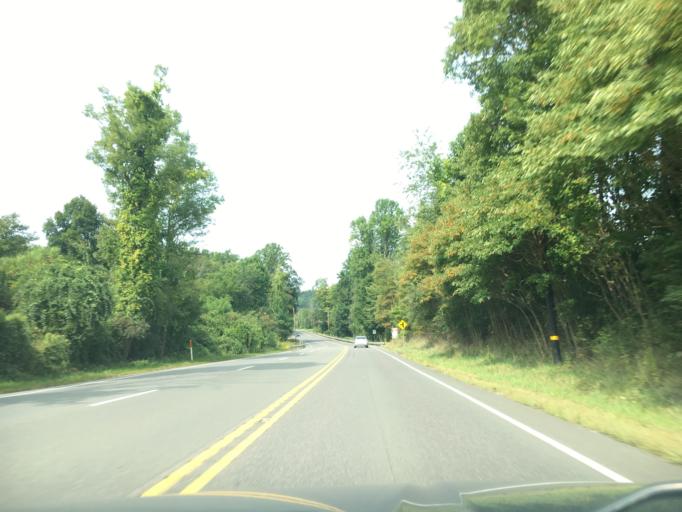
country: US
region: Pennsylvania
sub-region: Carbon County
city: Summit Hill
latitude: 40.7152
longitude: -75.8435
